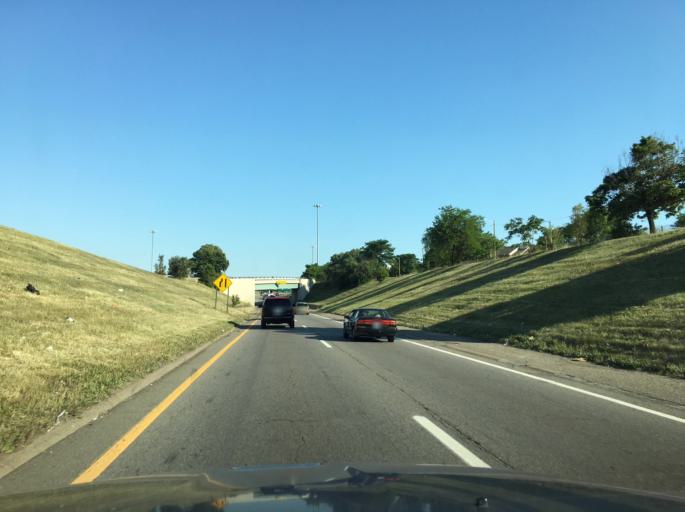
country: US
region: Michigan
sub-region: Wayne County
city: Hamtramck
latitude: 42.3647
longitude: -83.0571
